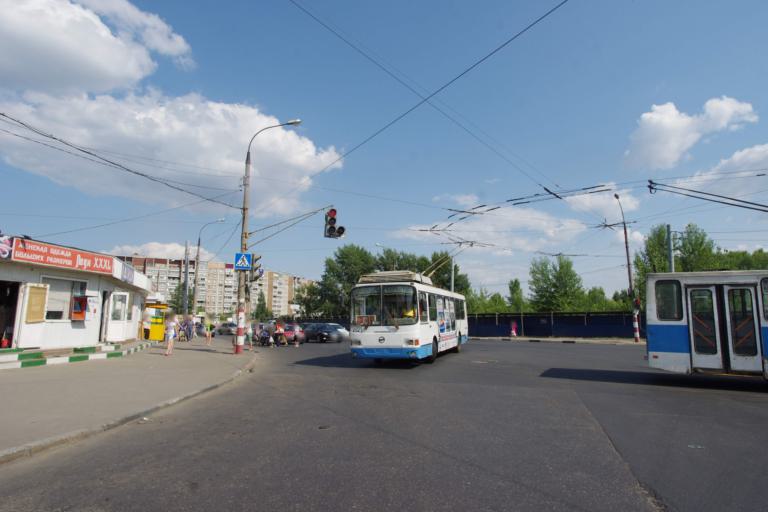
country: RU
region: Nizjnij Novgorod
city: Nizhniy Novgorod
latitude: 56.3435
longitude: 43.9310
